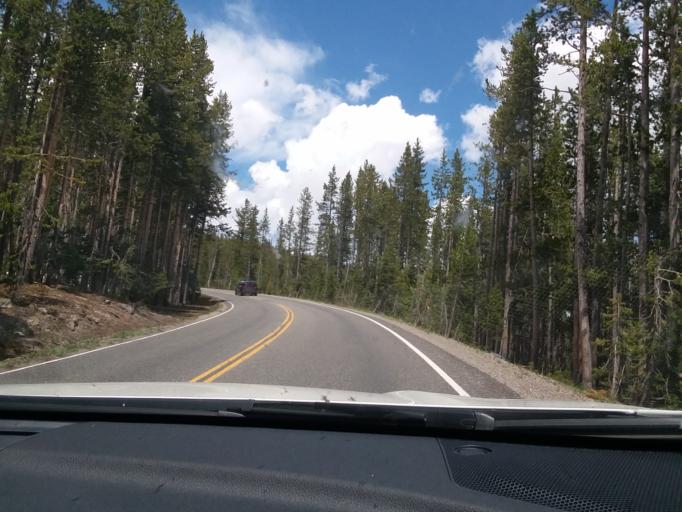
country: US
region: Montana
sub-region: Gallatin County
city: West Yellowstone
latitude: 44.1910
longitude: -110.6559
